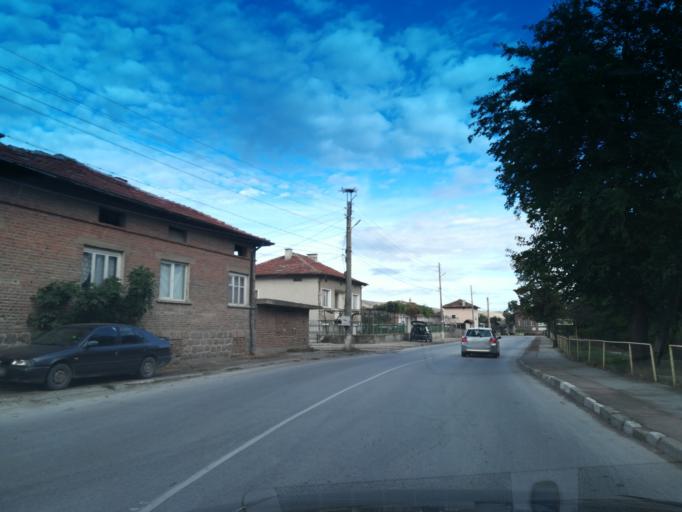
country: BG
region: Plovdiv
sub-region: Obshtina Krichim
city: Krichim
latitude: 42.0853
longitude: 24.4291
